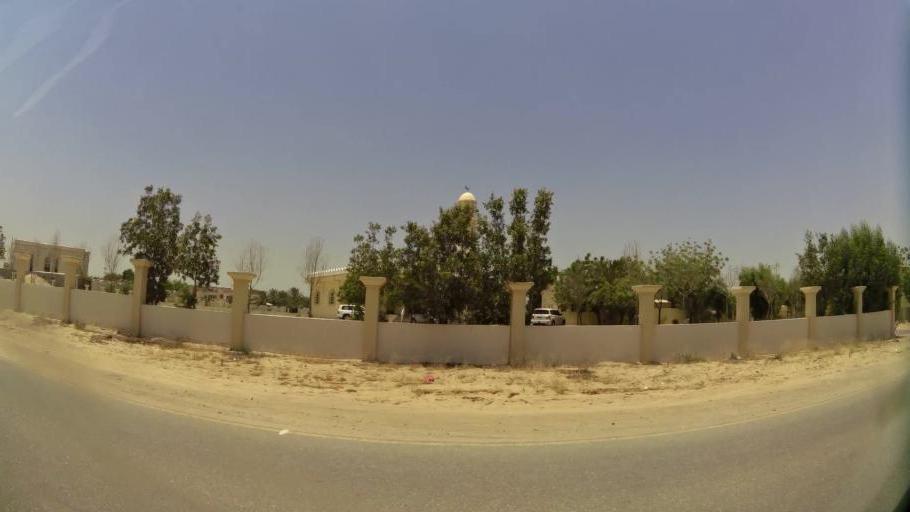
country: AE
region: Ajman
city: Ajman
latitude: 25.4056
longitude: 55.4945
